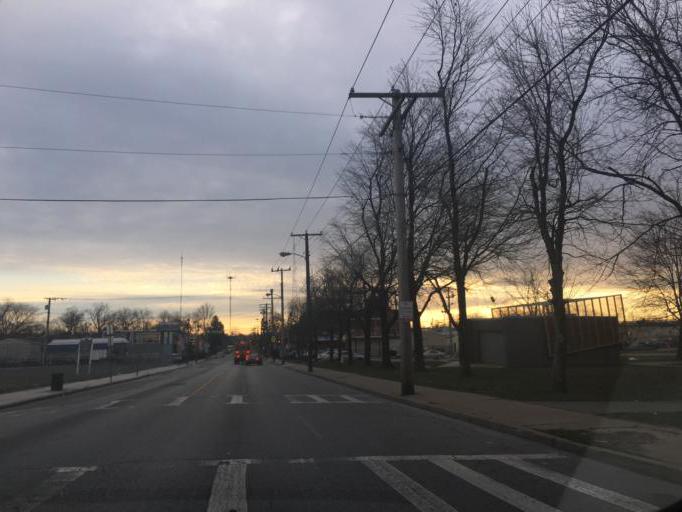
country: US
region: Maryland
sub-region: Baltimore County
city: Lochearn
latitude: 39.3414
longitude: -76.6752
